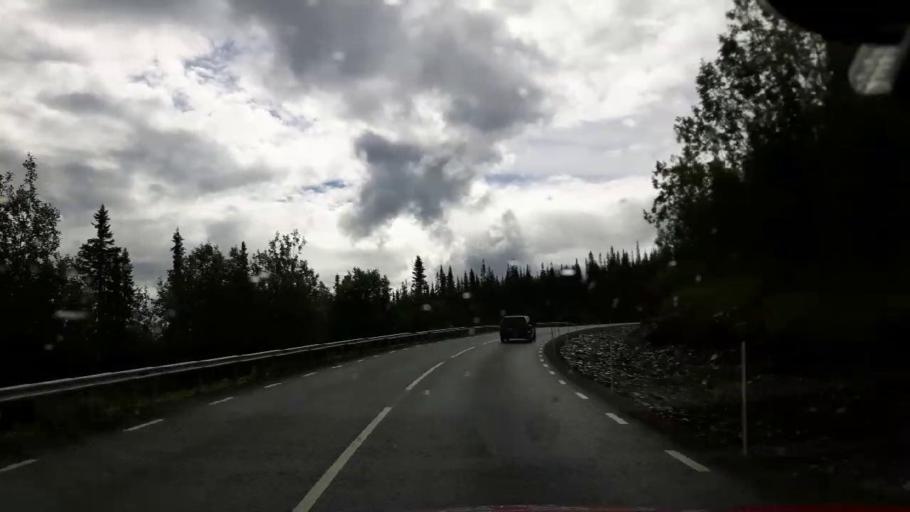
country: NO
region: Nord-Trondelag
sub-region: Royrvik
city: Royrvik
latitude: 64.8502
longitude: 14.1786
